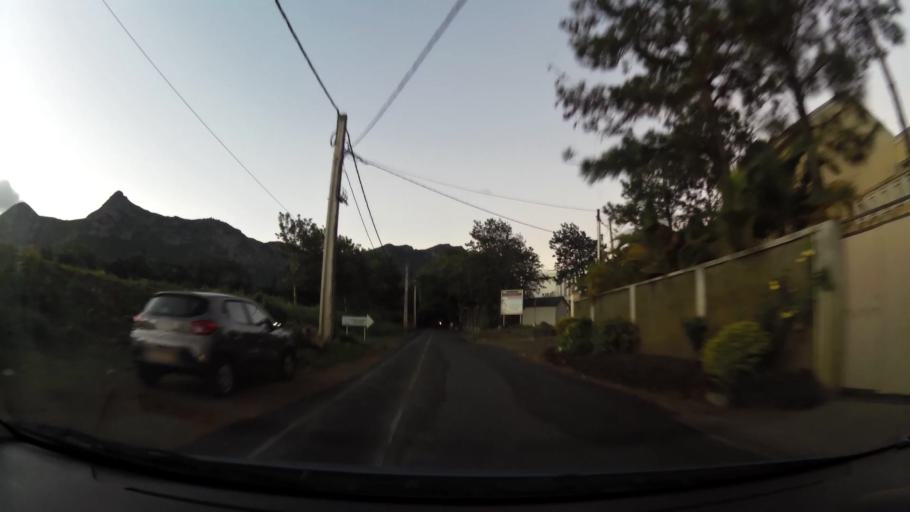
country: MU
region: Moka
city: Moka
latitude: -20.2247
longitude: 57.5000
